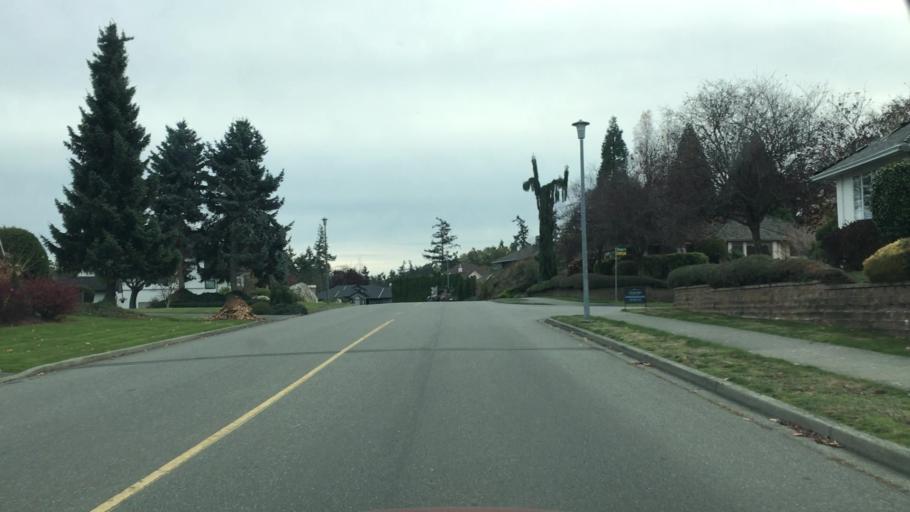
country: CA
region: British Columbia
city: Victoria
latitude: 48.5041
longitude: -123.3605
